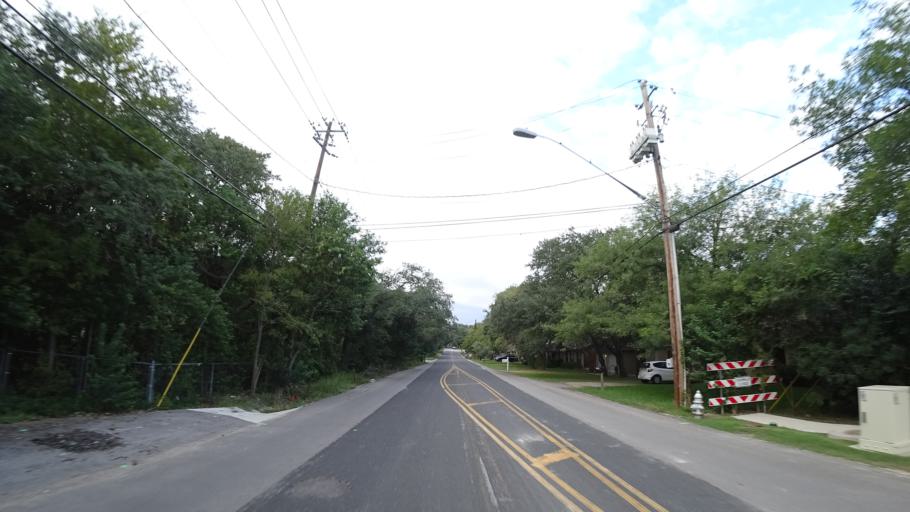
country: US
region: Texas
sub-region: Travis County
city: Onion Creek
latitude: 30.1903
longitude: -97.7942
